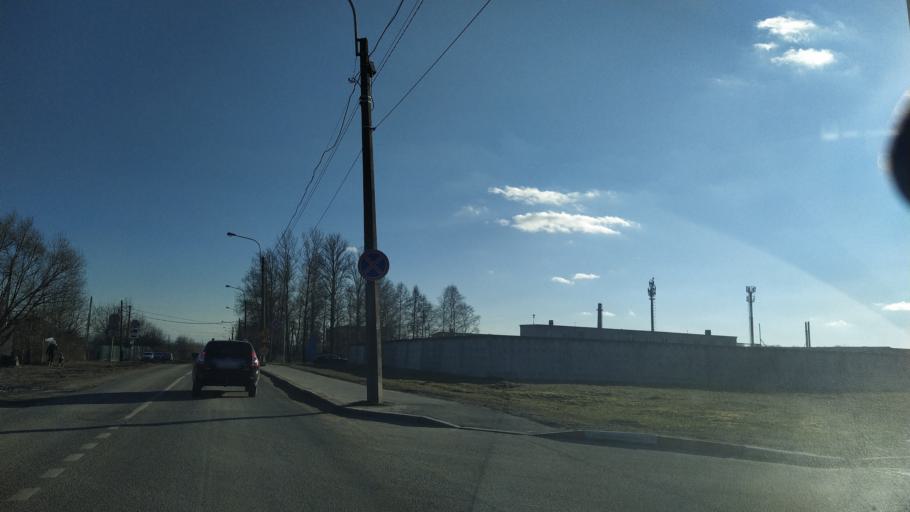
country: RU
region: St.-Petersburg
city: Pushkin
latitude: 59.6993
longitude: 30.3946
